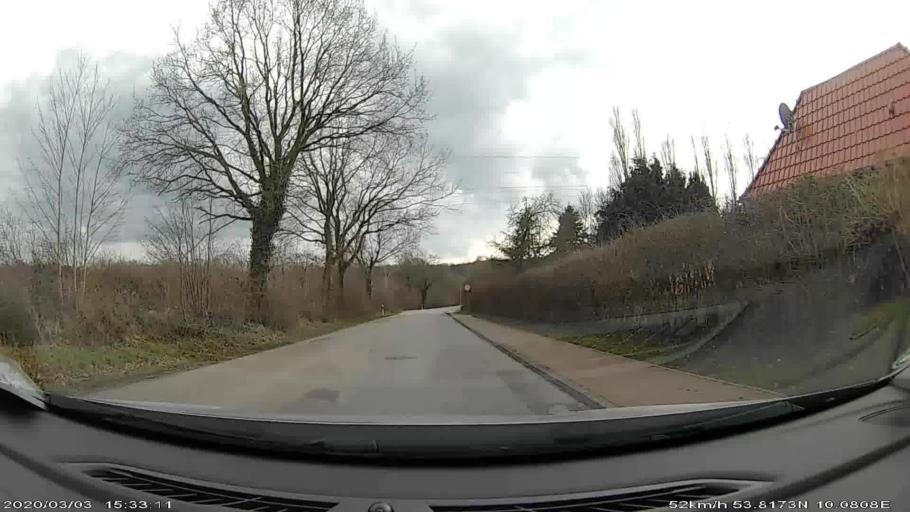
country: DE
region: Schleswig-Holstein
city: Huttblek
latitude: 53.8180
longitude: 10.0808
